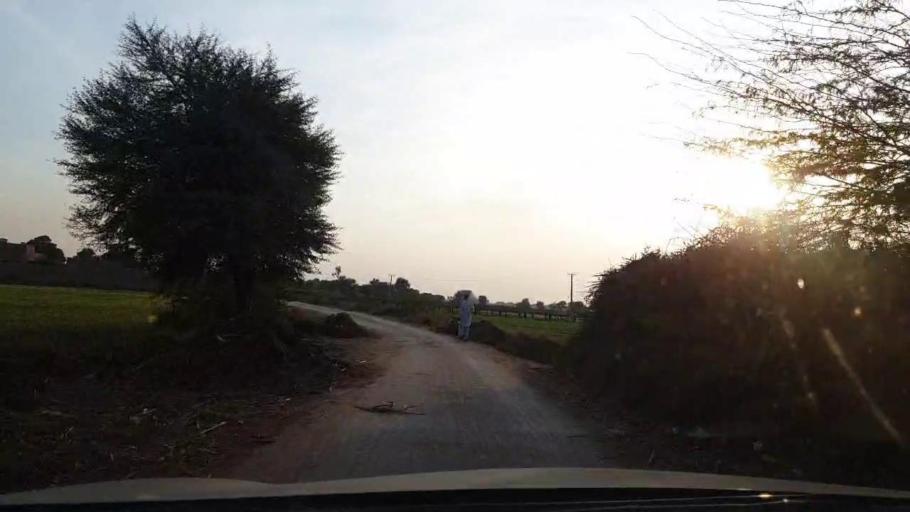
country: PK
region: Sindh
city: Tando Adam
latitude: 25.7129
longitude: 68.7214
